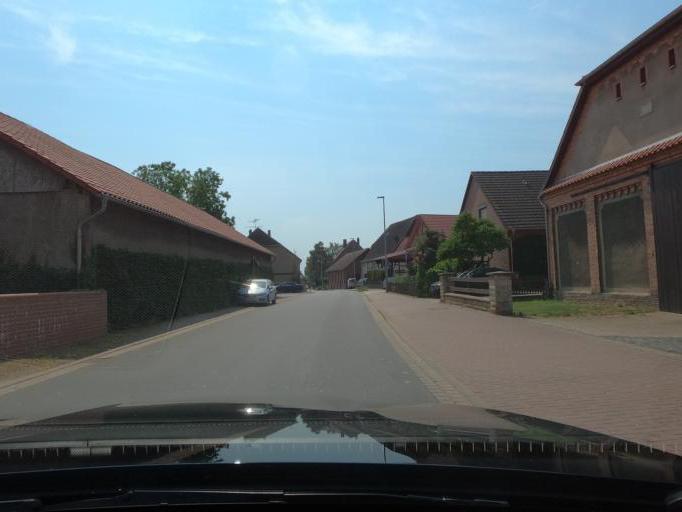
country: DE
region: Lower Saxony
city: Sarstedt
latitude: 52.2367
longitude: 9.8195
